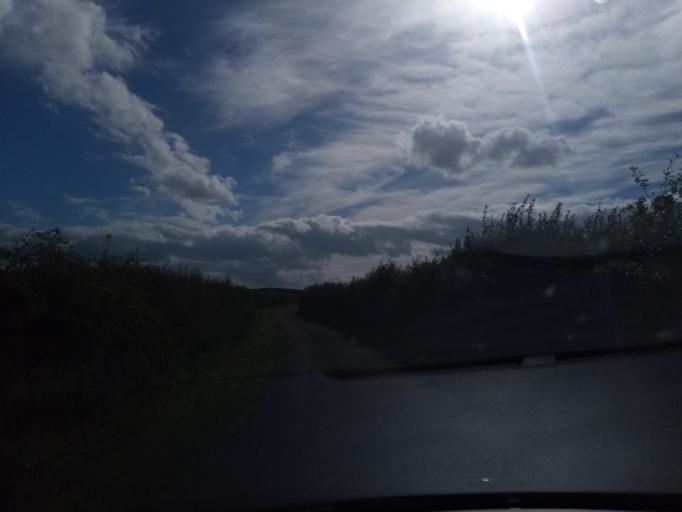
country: GB
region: England
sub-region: Northumberland
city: Kirknewton
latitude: 55.6116
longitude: -2.1748
